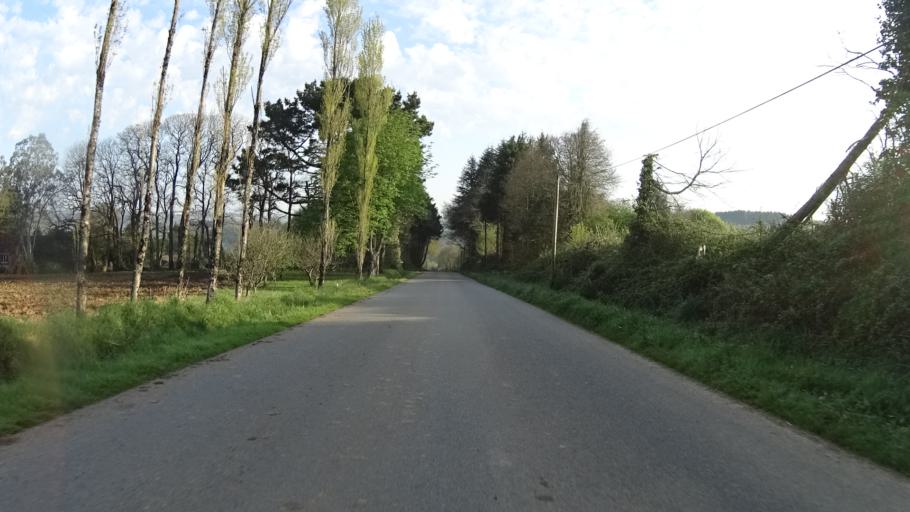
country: FR
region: Brittany
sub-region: Departement du Finistere
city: Sizun
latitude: 48.4308
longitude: -4.0717
